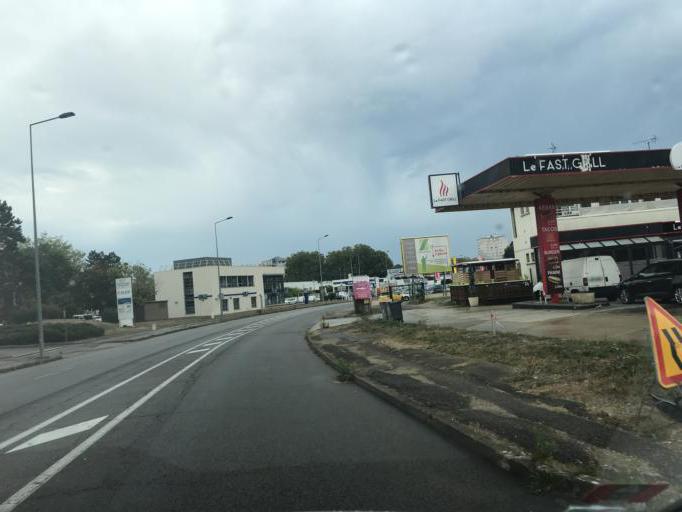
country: FR
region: Rhone-Alpes
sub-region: Departement de l'Ain
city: Bourg-en-Bresse
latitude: 46.2140
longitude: 5.2170
